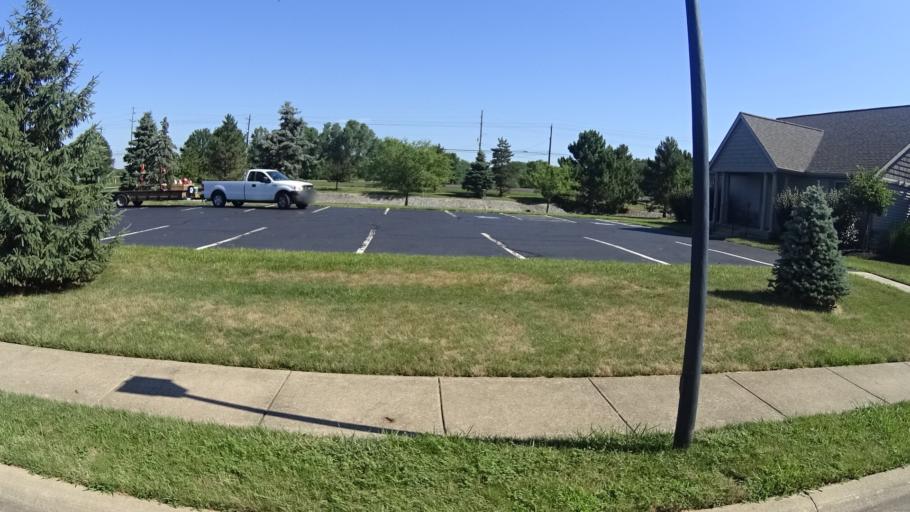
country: US
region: Ohio
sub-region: Erie County
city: Sandusky
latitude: 41.3951
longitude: -82.6414
